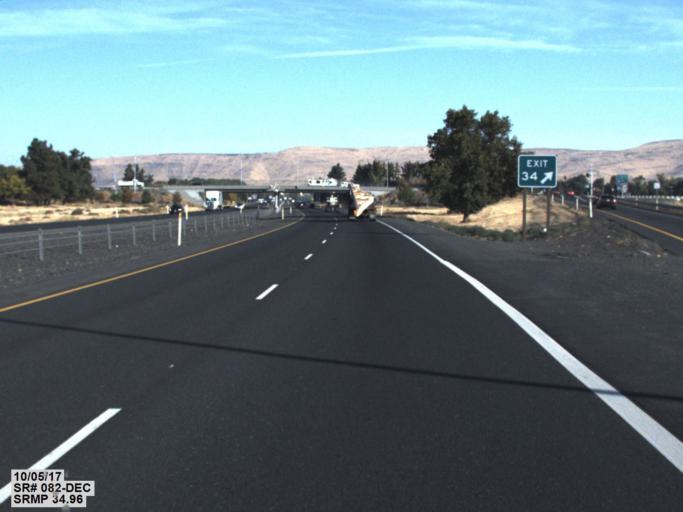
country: US
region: Washington
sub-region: Yakima County
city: Union Gap
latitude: 46.5823
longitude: -120.4720
